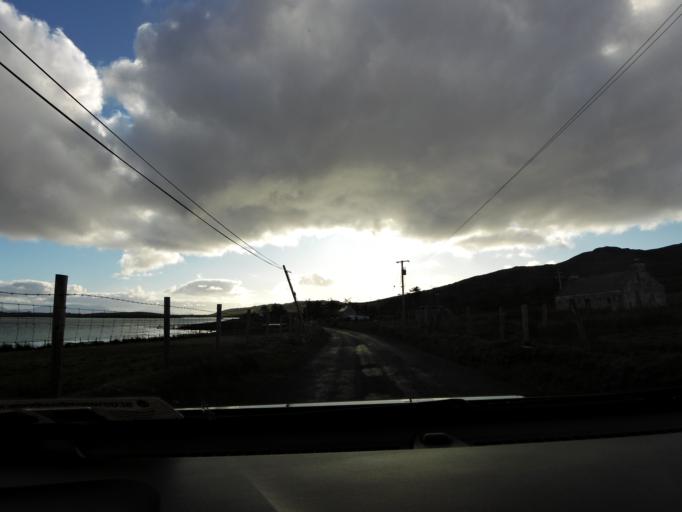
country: IE
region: Connaught
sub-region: Maigh Eo
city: Belmullet
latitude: 53.8888
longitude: -9.9431
